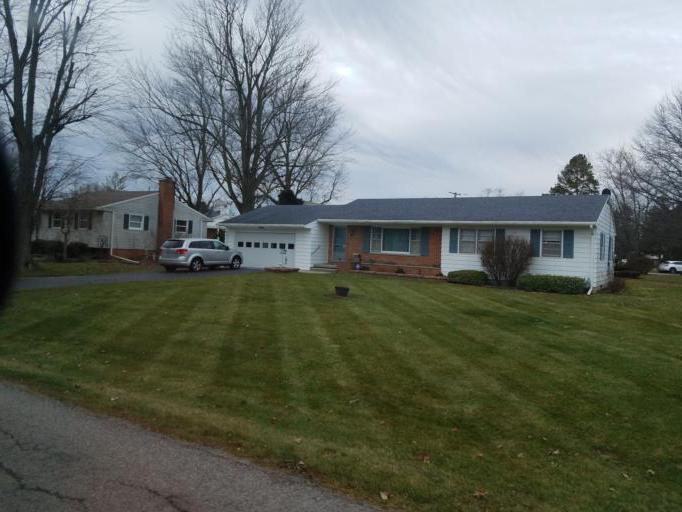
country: US
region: Ohio
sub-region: Marion County
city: Marion
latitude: 40.5757
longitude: -83.0970
